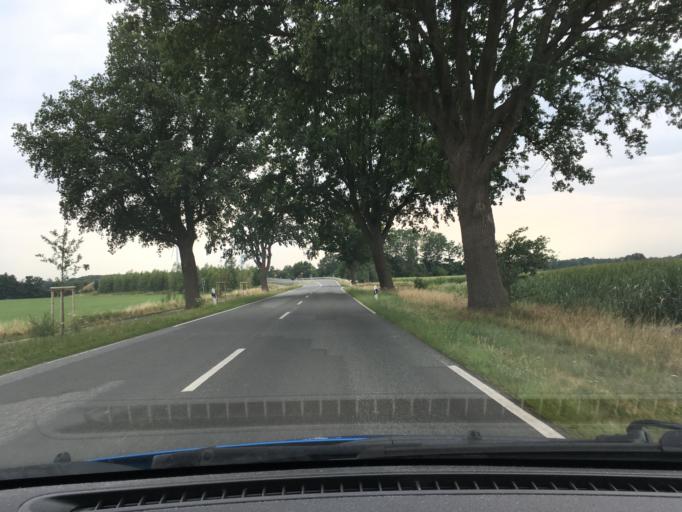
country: DE
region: Lower Saxony
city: Adelheidsdorf
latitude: 52.5389
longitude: 10.0502
